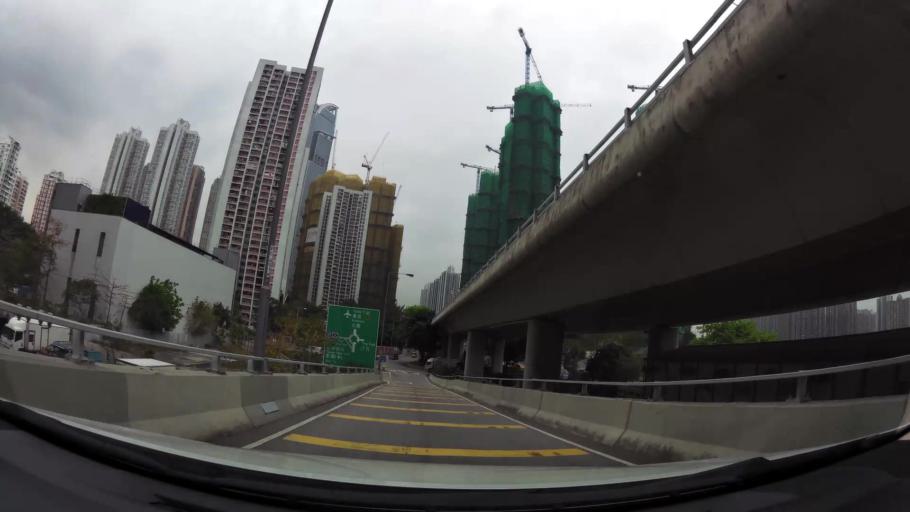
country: HK
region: Tsuen Wan
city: Tsuen Wan
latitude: 22.3716
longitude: 114.1079
